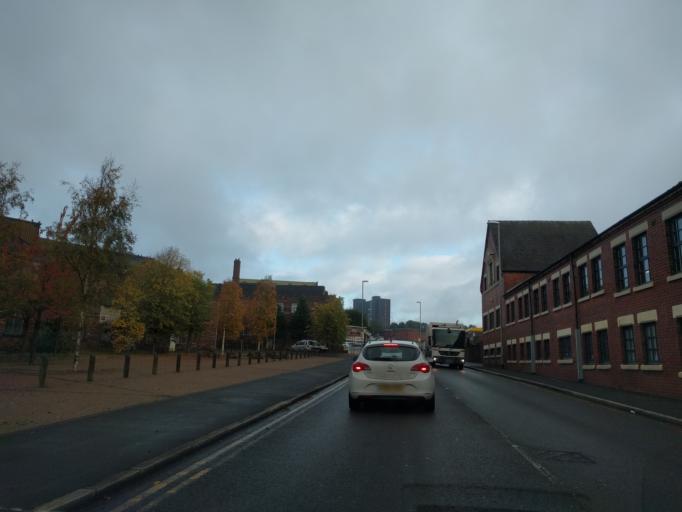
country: GB
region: England
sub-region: Stoke-on-Trent
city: Stoke-on-Trent
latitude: 53.0191
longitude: -2.1712
